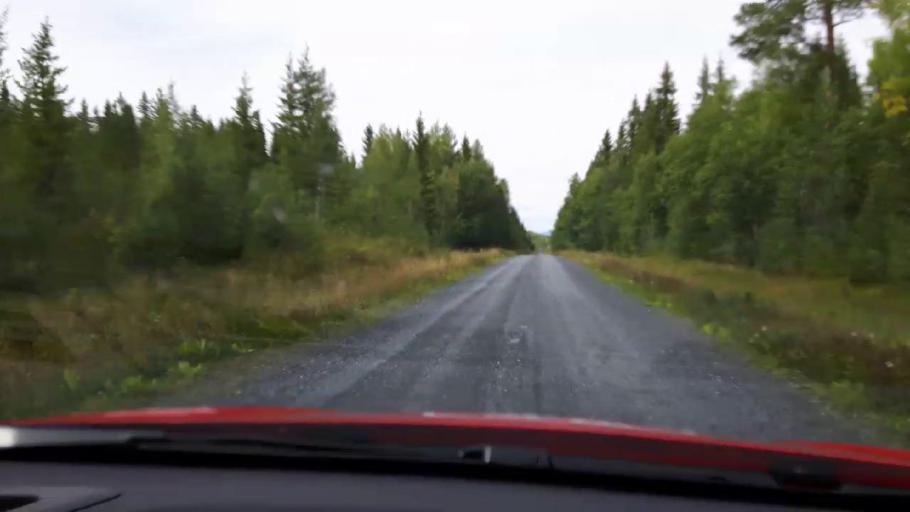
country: SE
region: Jaemtland
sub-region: Krokoms Kommun
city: Valla
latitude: 63.2690
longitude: 13.7656
